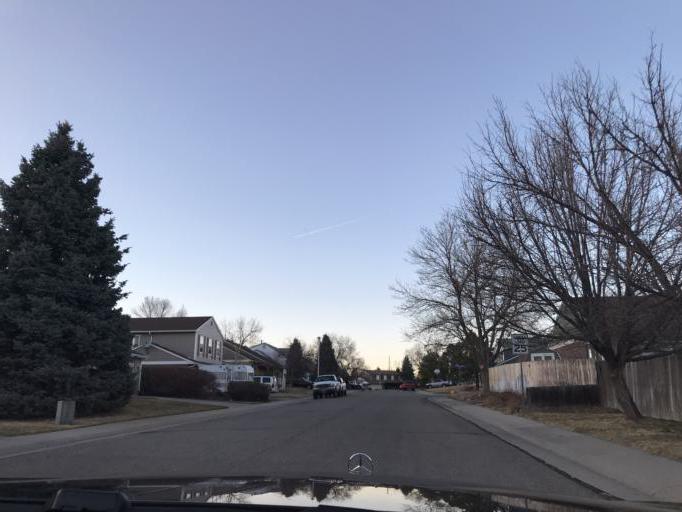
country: US
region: Colorado
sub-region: Jefferson County
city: Applewood
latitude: 39.8246
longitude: -105.1626
